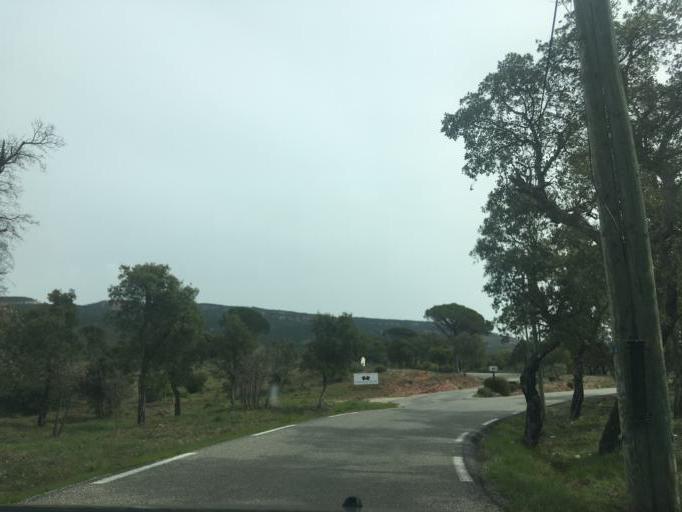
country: FR
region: Provence-Alpes-Cote d'Azur
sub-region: Departement du Var
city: Le Muy
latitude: 43.5123
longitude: 6.6150
